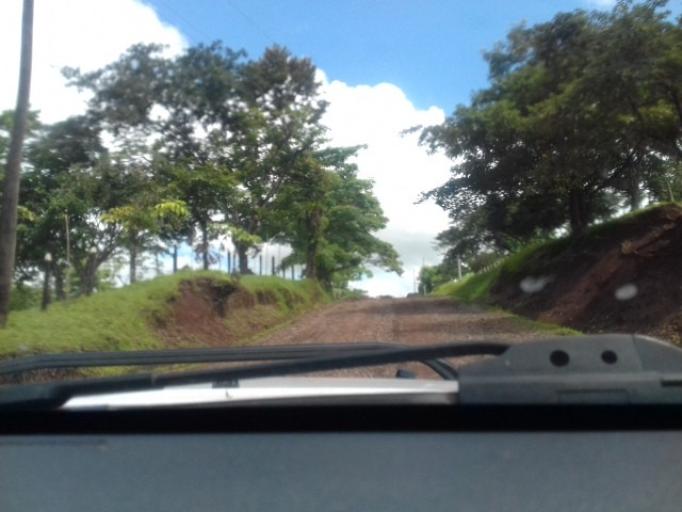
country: NI
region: Matagalpa
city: Rio Blanco
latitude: 12.9785
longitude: -85.1848
